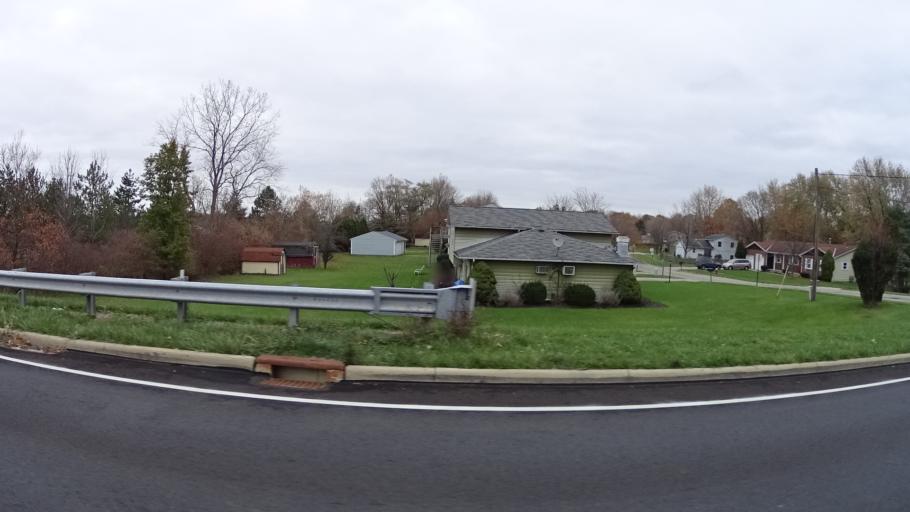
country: US
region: Ohio
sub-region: Lorain County
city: Sheffield
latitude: 41.4152
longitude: -82.0924
